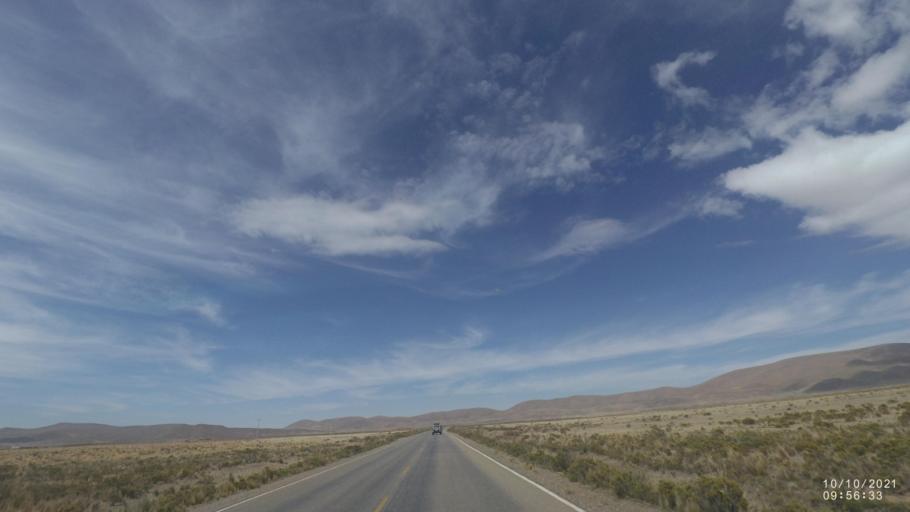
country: BO
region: La Paz
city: Colquiri
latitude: -17.3239
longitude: -67.3761
